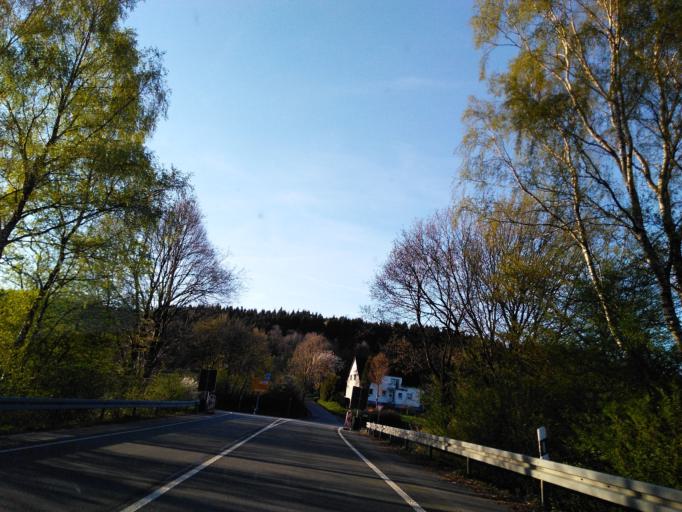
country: DE
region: North Rhine-Westphalia
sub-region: Regierungsbezirk Arnsberg
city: Herscheid
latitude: 51.1577
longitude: 7.7432
